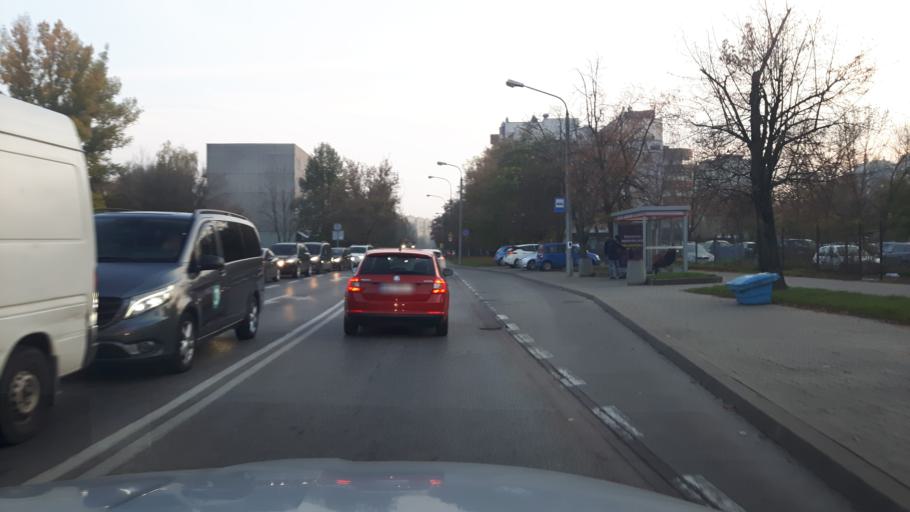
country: PL
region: Masovian Voivodeship
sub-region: Warszawa
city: Mokotow
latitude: 52.1832
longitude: 21.0141
